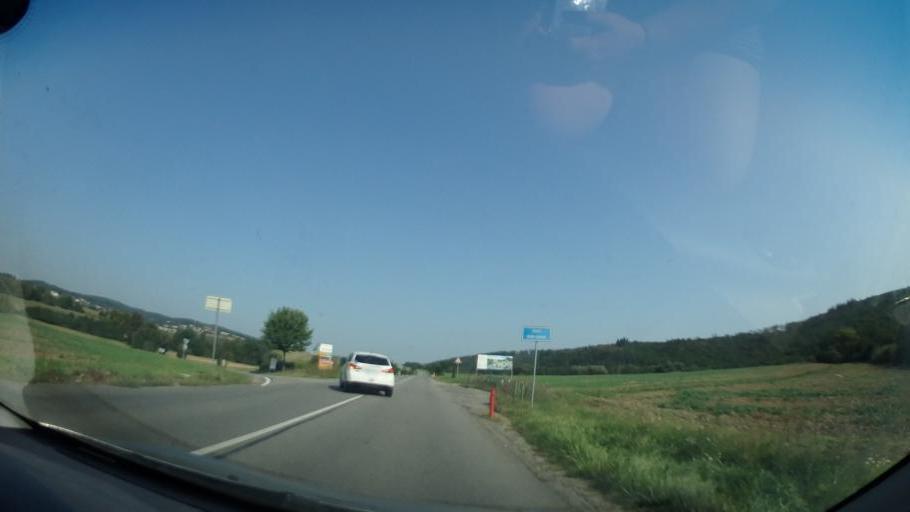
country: CZ
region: South Moravian
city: Kurim
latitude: 49.2407
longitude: 16.5304
